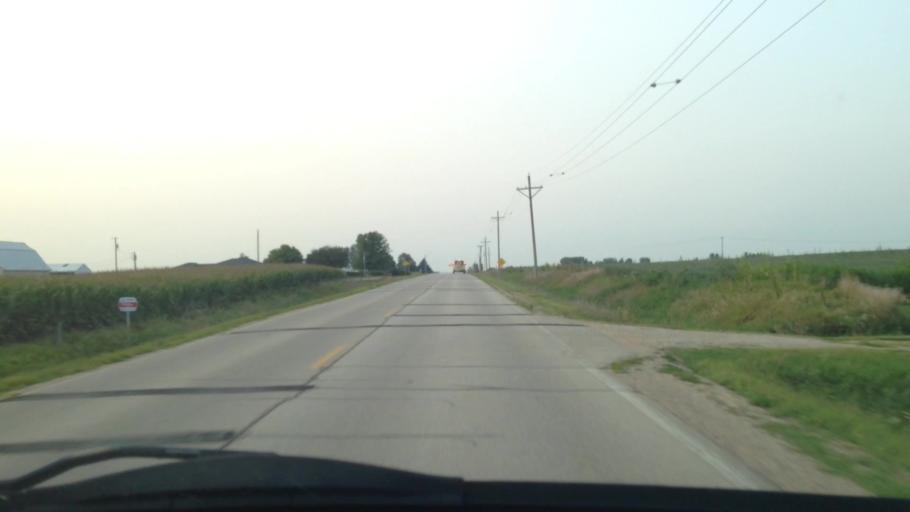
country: US
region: Iowa
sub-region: Benton County
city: Atkins
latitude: 41.9894
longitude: -91.8732
